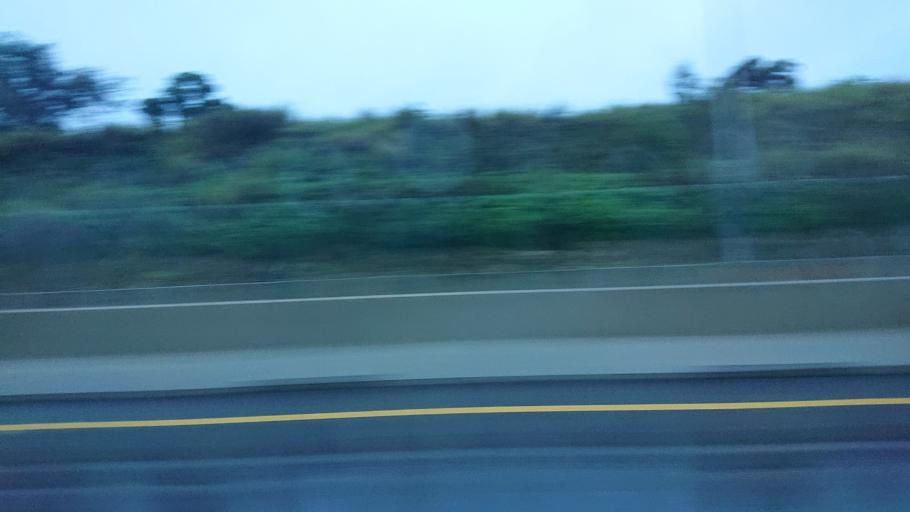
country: TW
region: Taiwan
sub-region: Miaoli
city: Miaoli
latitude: 24.5633
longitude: 120.7147
